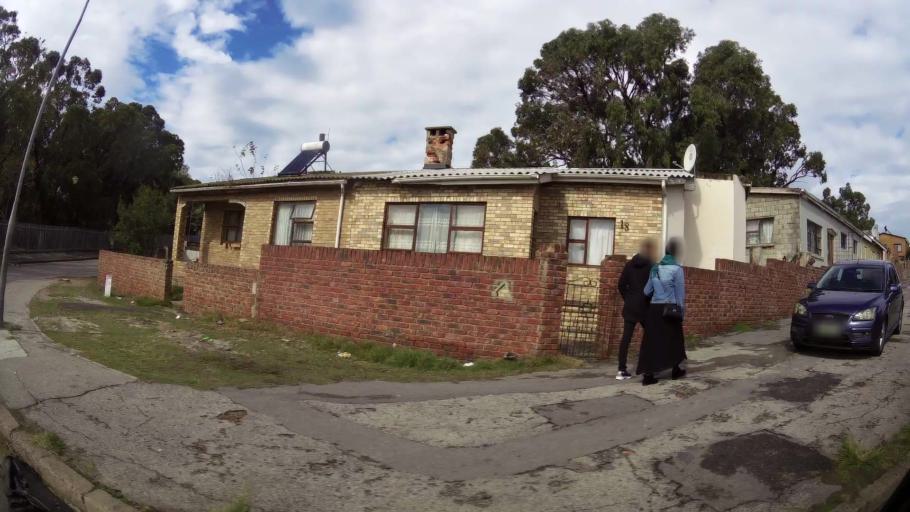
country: ZA
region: Eastern Cape
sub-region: Nelson Mandela Bay Metropolitan Municipality
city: Port Elizabeth
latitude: -33.9297
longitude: 25.5654
